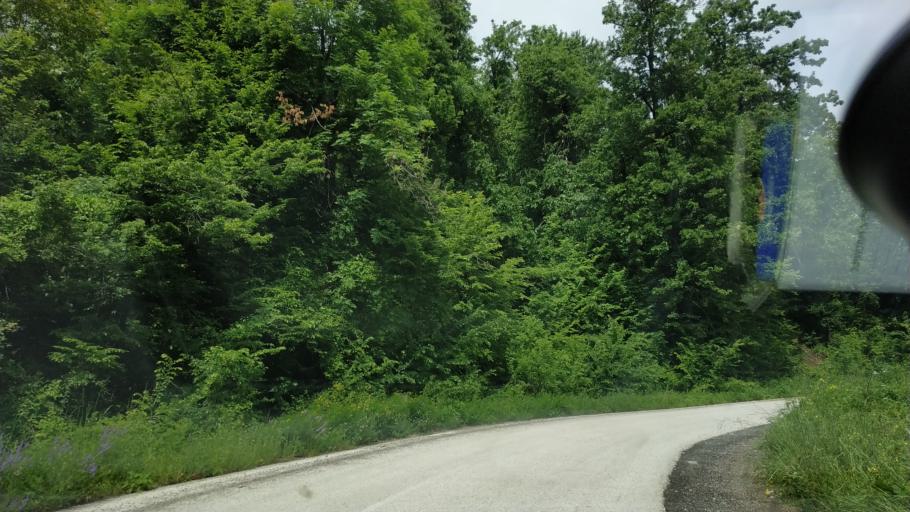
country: RS
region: Central Serbia
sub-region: Zajecarski Okrug
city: Boljevac
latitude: 43.7368
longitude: 21.9509
